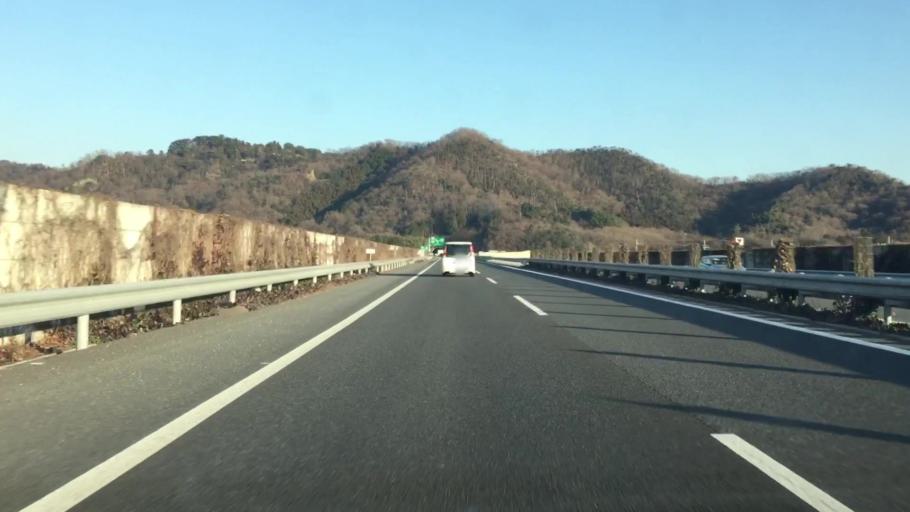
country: JP
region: Tochigi
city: Tanuma
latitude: 36.3530
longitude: 139.5822
